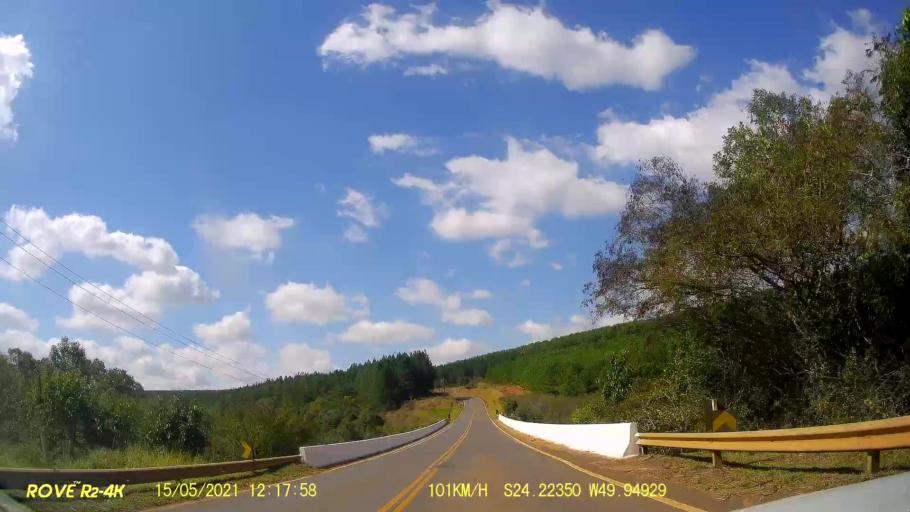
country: BR
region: Parana
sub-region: Jaguariaiva
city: Jaguariaiva
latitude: -24.2233
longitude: -49.9493
